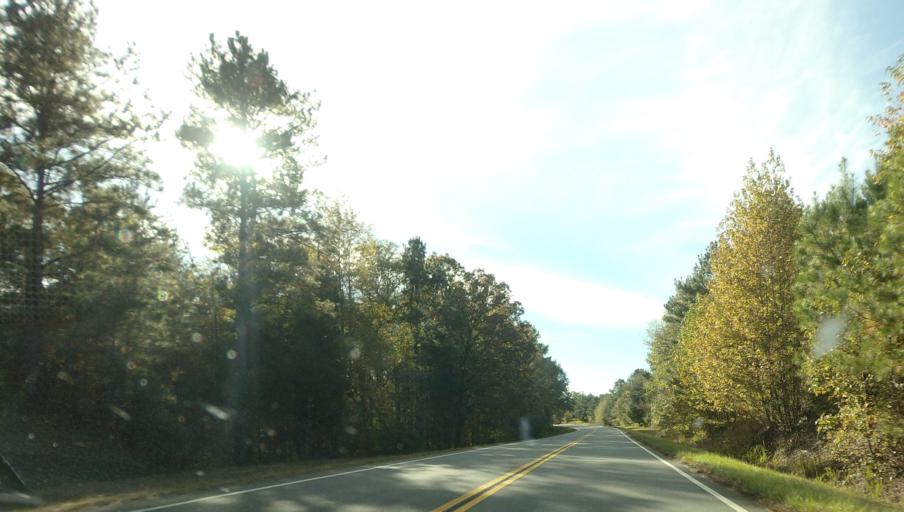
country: US
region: Georgia
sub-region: Talbot County
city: Talbotton
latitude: 32.7061
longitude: -84.3904
